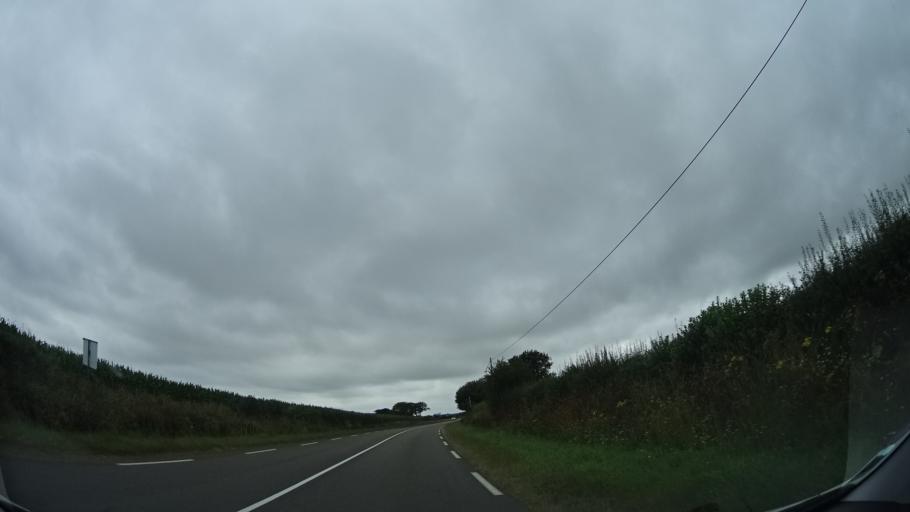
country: FR
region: Lower Normandy
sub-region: Departement de la Manche
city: La Haye-du-Puits
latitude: 49.3115
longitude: -1.6053
